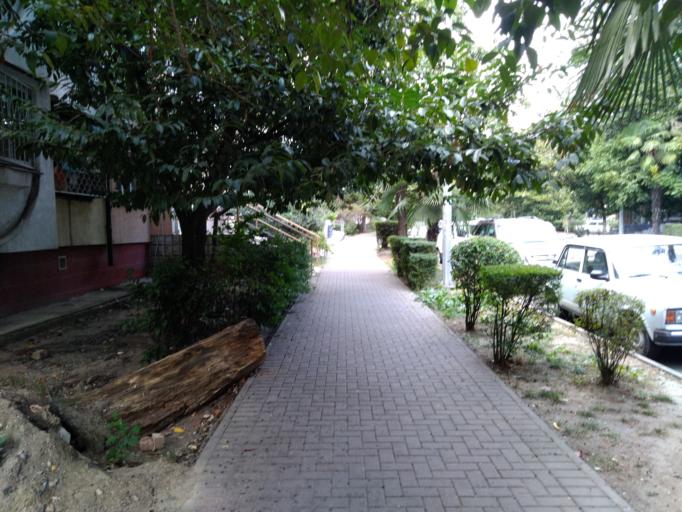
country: RU
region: Krasnodarskiy
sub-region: Sochi City
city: Sochi
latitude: 43.5986
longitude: 39.7213
